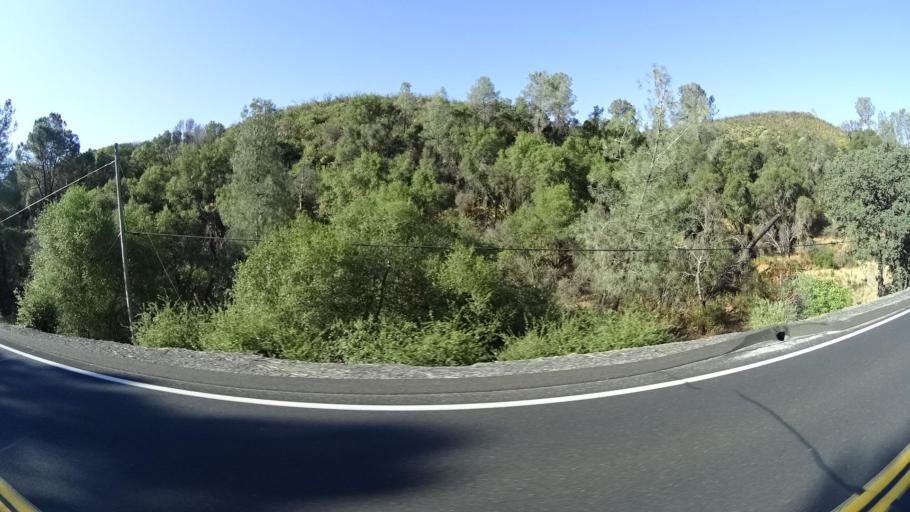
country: US
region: California
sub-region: Mariposa County
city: Mariposa
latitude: 37.5147
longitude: -120.0521
